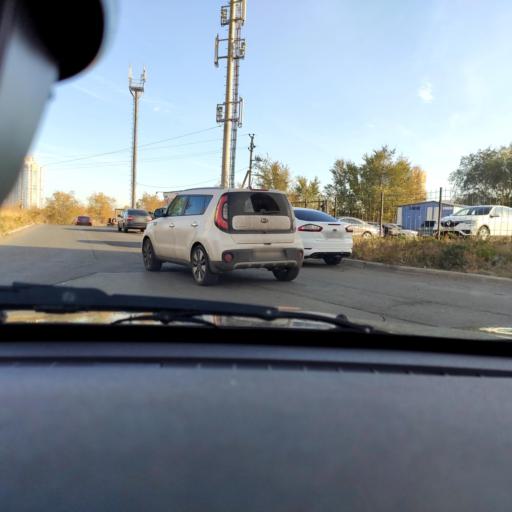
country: RU
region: Samara
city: Tol'yatti
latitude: 53.5078
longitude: 49.2524
